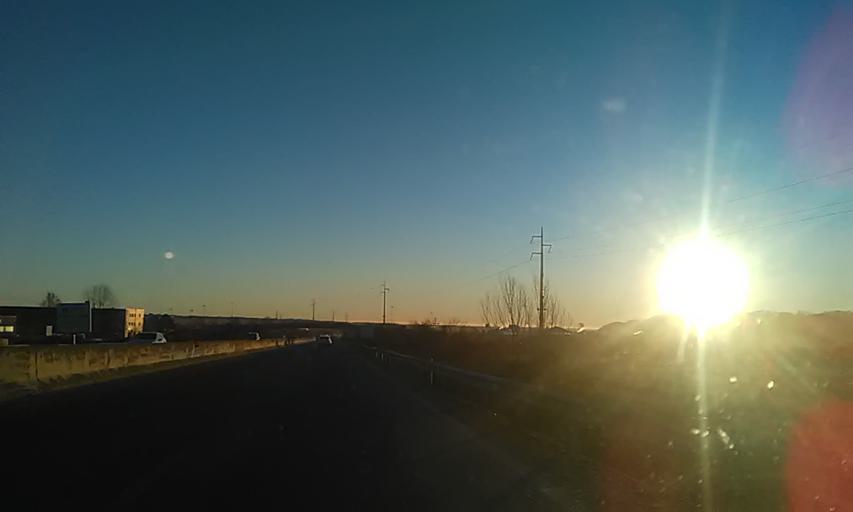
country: IT
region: Piedmont
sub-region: Provincia di Biella
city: Vigliano Biellese
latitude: 45.5553
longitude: 8.1226
